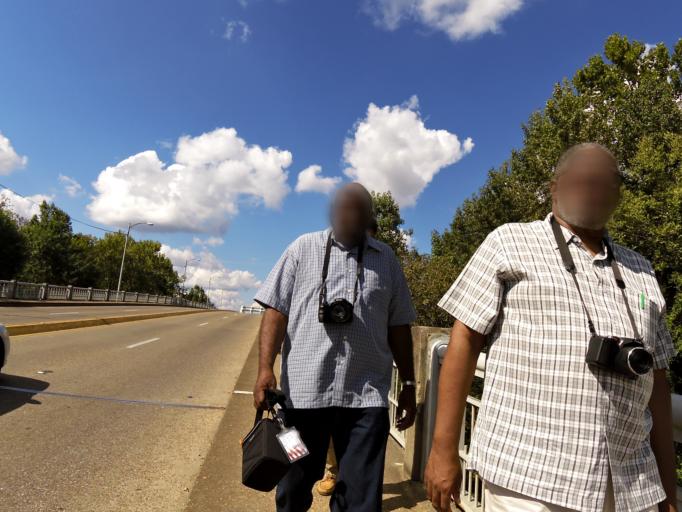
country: US
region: Alabama
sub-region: Dallas County
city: Selma
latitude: 32.4035
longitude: -87.0173
